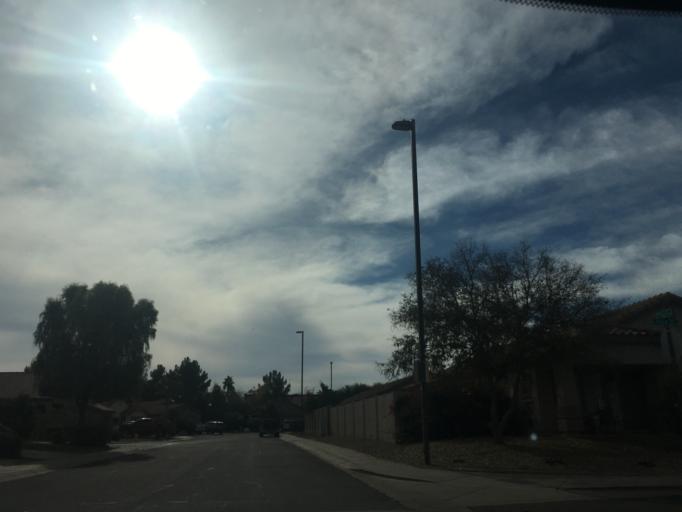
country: US
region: Arizona
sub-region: Maricopa County
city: Gilbert
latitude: 33.3530
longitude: -111.8078
